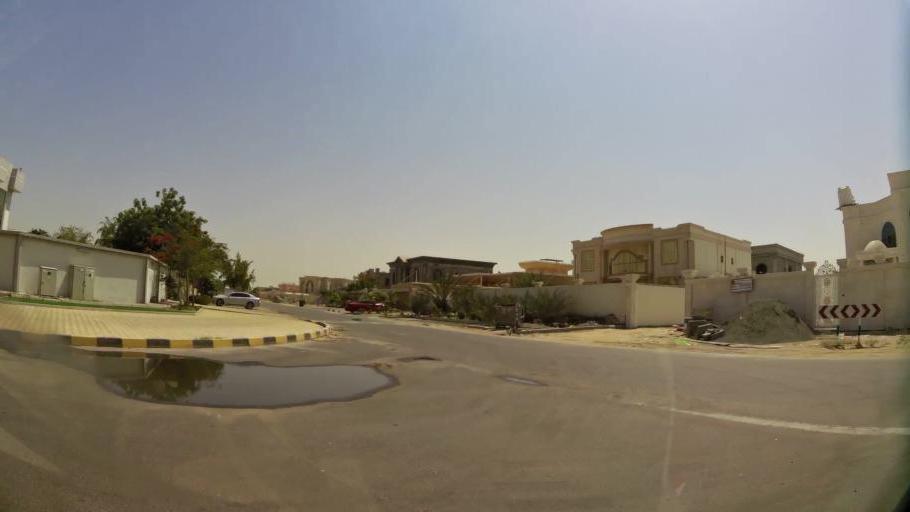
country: AE
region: Ajman
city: Ajman
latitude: 25.4206
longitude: 55.5214
